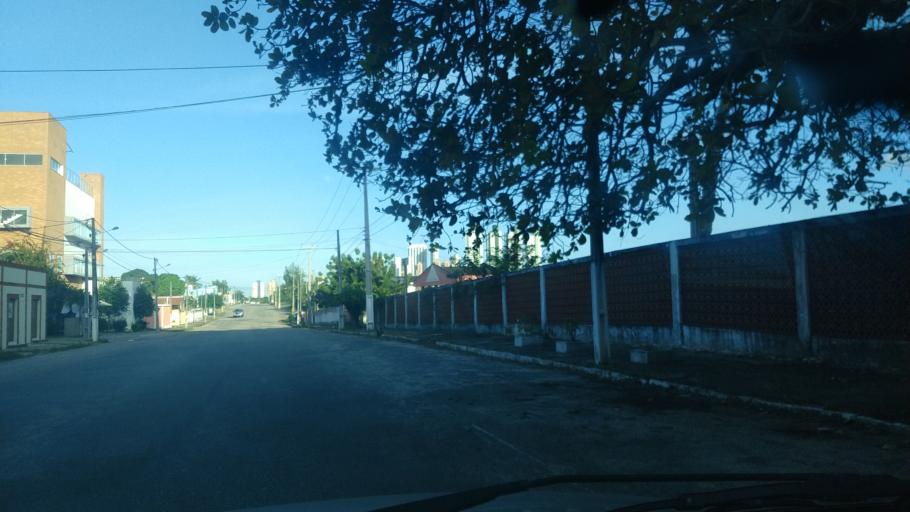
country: BR
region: Rio Grande do Norte
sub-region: Natal
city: Natal
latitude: -5.8729
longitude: -35.1890
